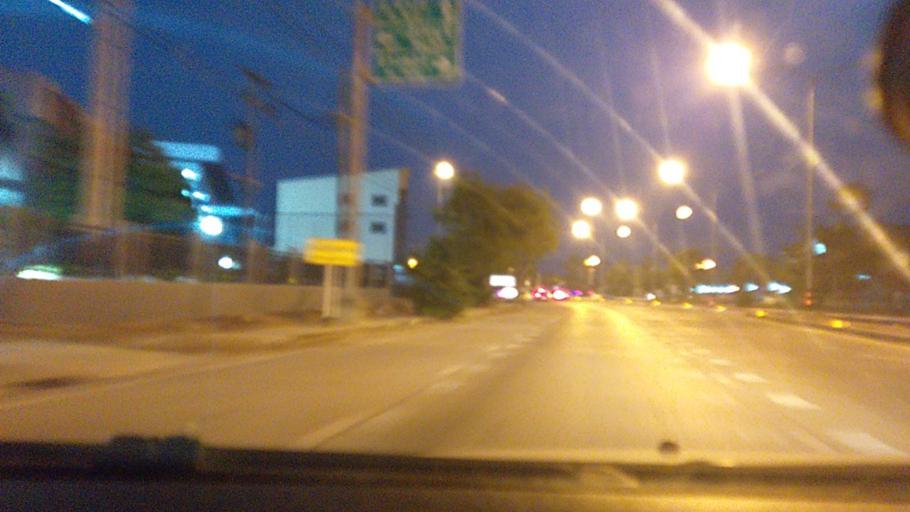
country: TH
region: Sing Buri
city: Sing Buri
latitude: 14.8704
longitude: 100.4039
